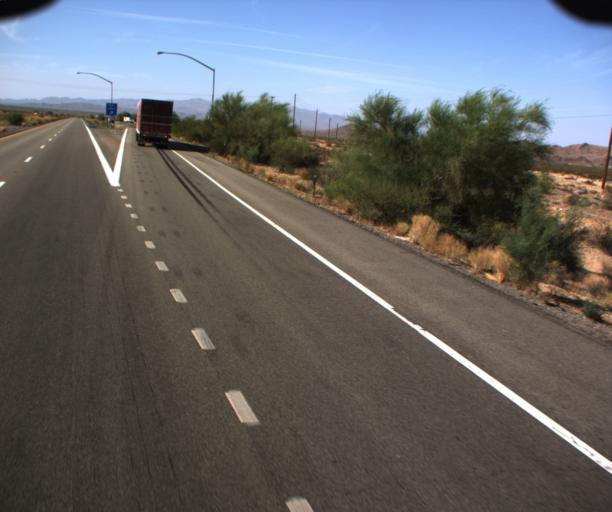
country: US
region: Arizona
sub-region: Mohave County
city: Desert Hills
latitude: 34.8356
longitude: -114.1454
